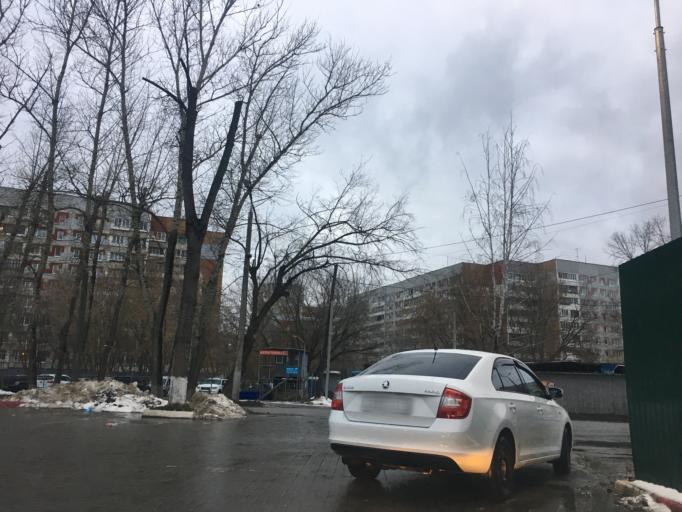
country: RU
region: Tula
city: Tula
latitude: 54.2088
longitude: 37.6269
